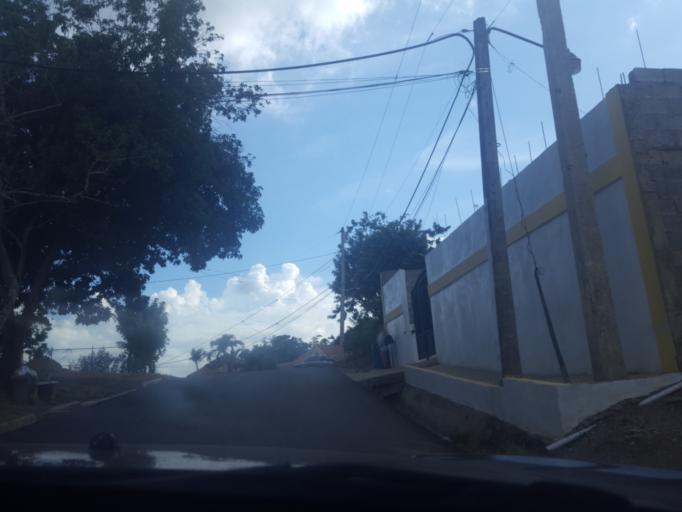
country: DO
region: Santiago
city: Licey al Medio
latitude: 19.3643
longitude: -70.6322
